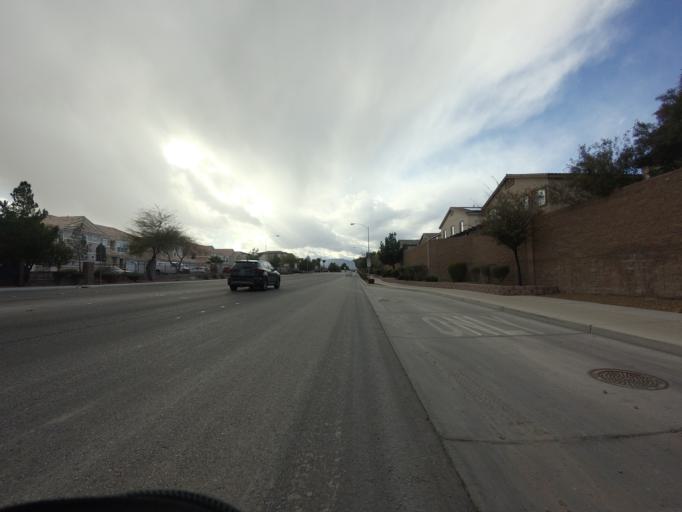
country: US
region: Nevada
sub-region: Clark County
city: North Las Vegas
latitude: 36.2690
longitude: -115.1987
